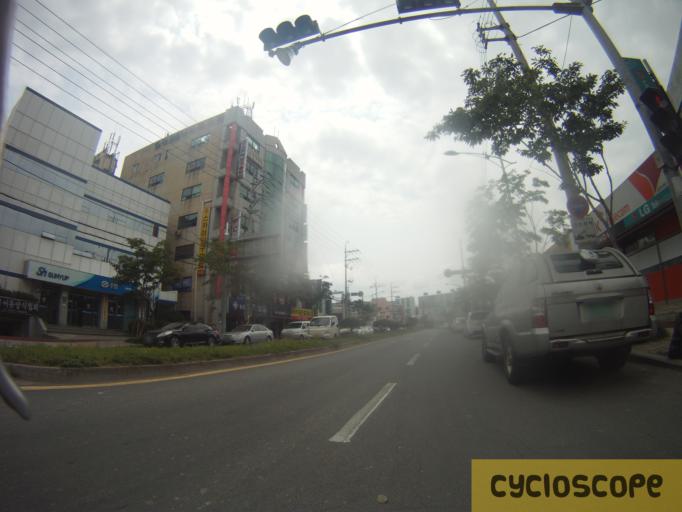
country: KR
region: Busan
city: Kijang
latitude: 35.2631
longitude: 129.2322
